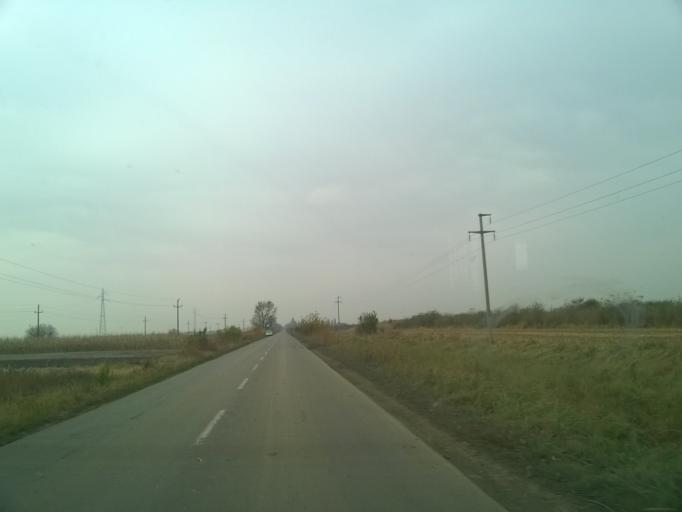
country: RS
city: Debeljaca
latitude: 45.0702
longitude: 20.6373
